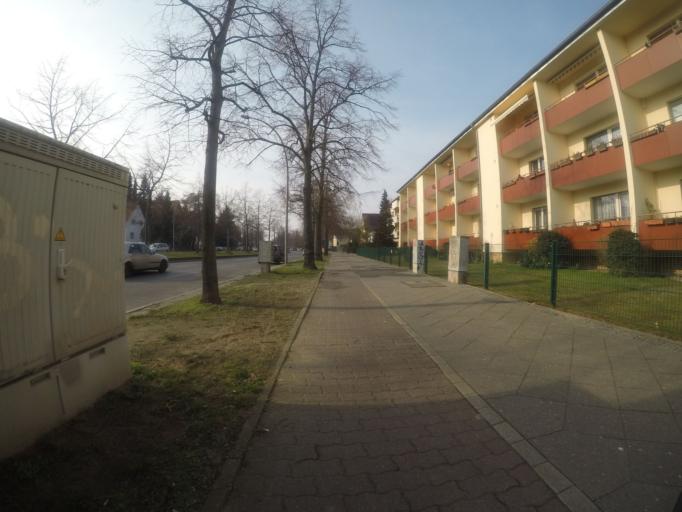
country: DE
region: Berlin
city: Rudow
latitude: 52.4303
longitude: 13.4774
